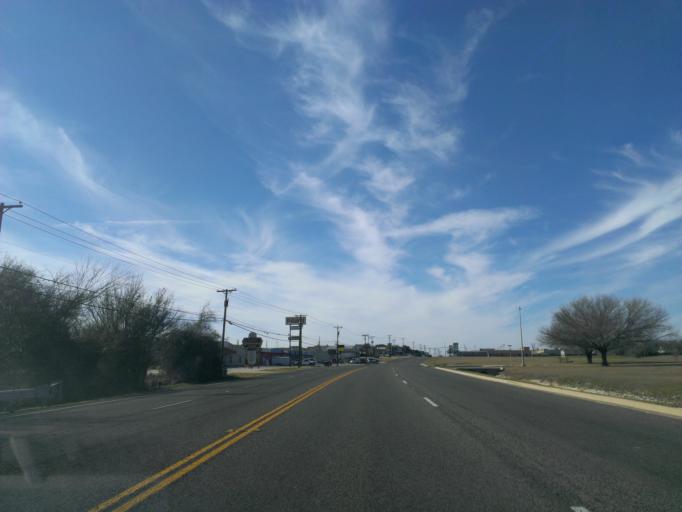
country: US
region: Texas
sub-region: Bell County
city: Killeen
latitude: 31.1162
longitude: -97.6894
